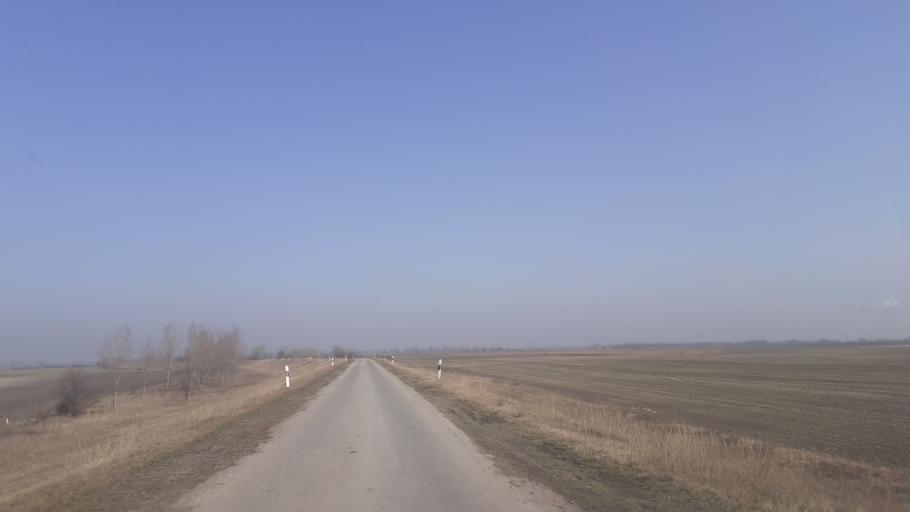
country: HU
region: Bacs-Kiskun
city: Tass
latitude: 47.0396
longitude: 18.9906
